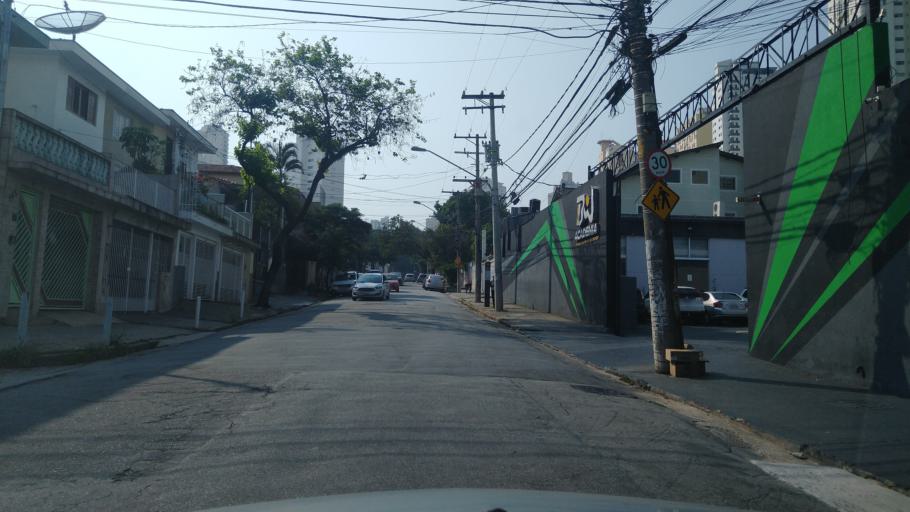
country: BR
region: Sao Paulo
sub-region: Sao Paulo
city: Sao Paulo
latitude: -23.4835
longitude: -46.6291
